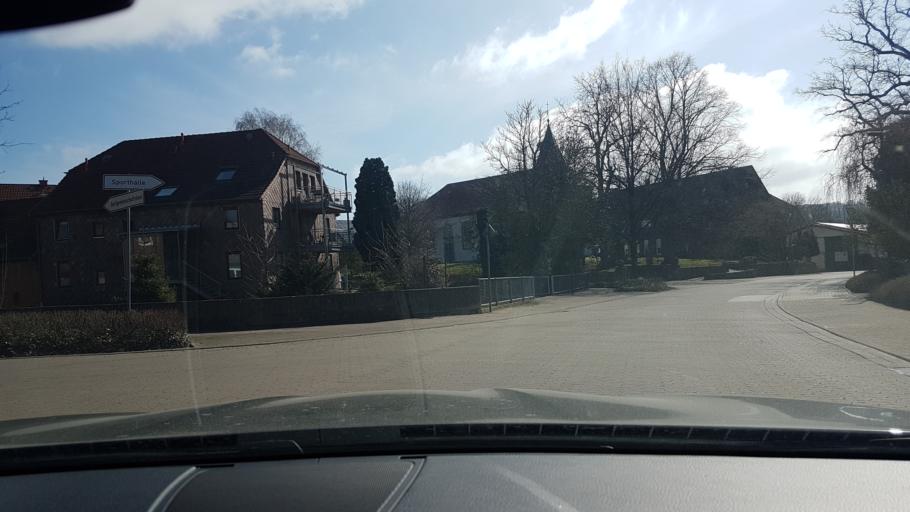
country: DE
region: Lower Saxony
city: Bad Munder am Deister
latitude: 52.1249
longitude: 9.4370
